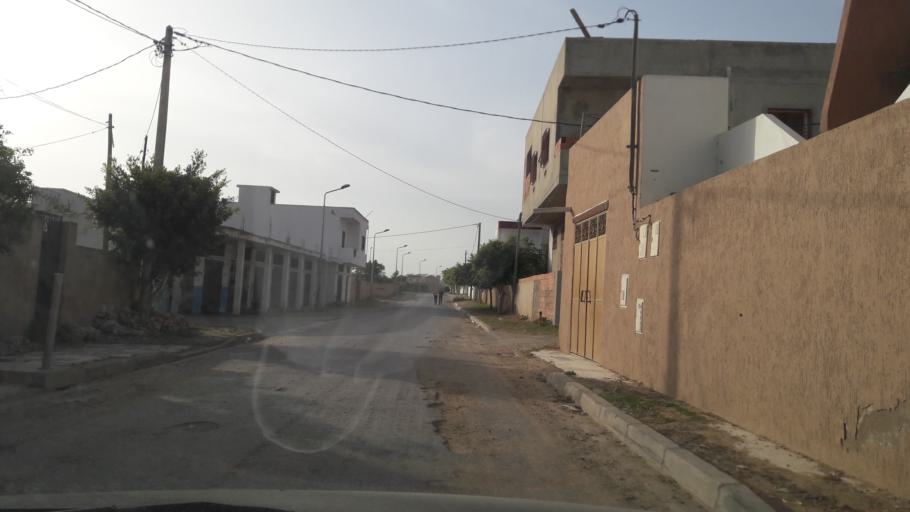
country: TN
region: Safaqis
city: Al Qarmadah
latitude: 34.7993
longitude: 10.7541
